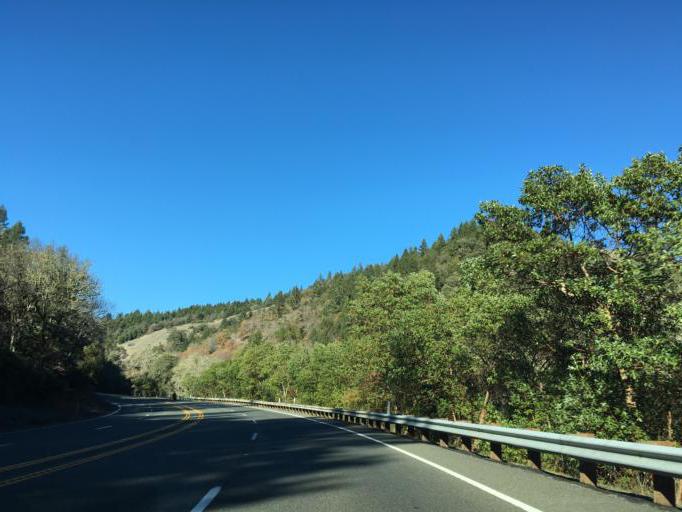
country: US
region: California
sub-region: Mendocino County
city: Laytonville
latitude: 39.6013
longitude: -123.4537
